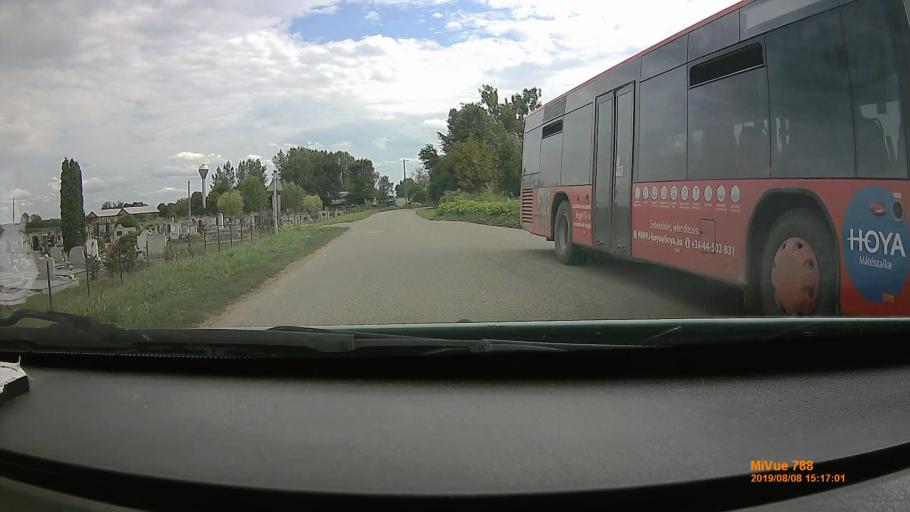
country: HU
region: Szabolcs-Szatmar-Bereg
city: Tunyogmatolcs
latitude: 47.9645
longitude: 22.4602
